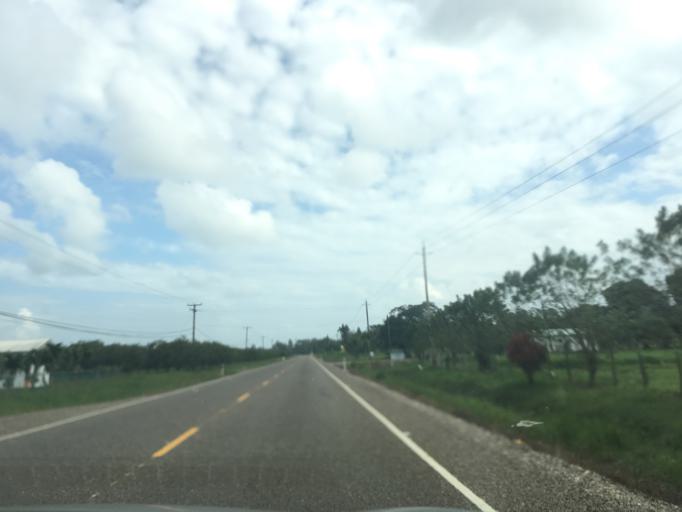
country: BZ
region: Stann Creek
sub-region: Dangriga
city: Dangriga
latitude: 16.9968
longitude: -88.3218
